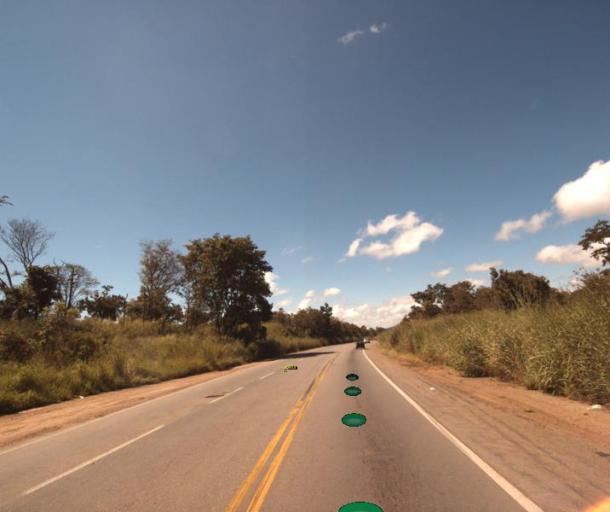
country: BR
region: Goias
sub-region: Jaragua
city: Jaragua
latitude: -15.6604
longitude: -49.3564
